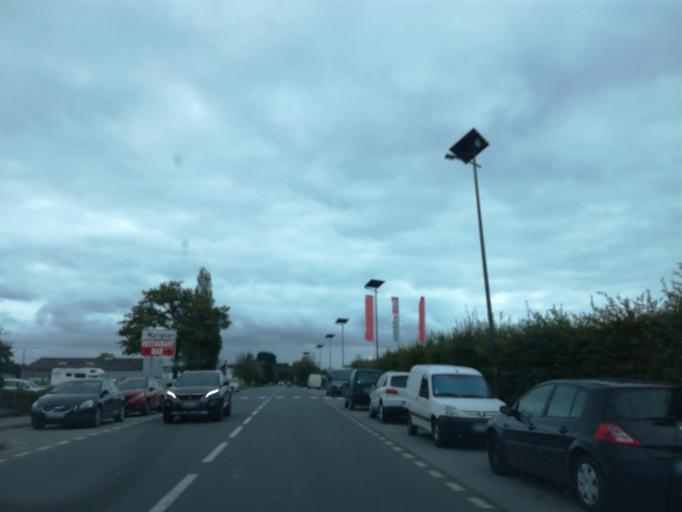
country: FR
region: Brittany
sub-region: Departement des Cotes-d'Armor
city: Loudeac
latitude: 48.1564
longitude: -2.7573
